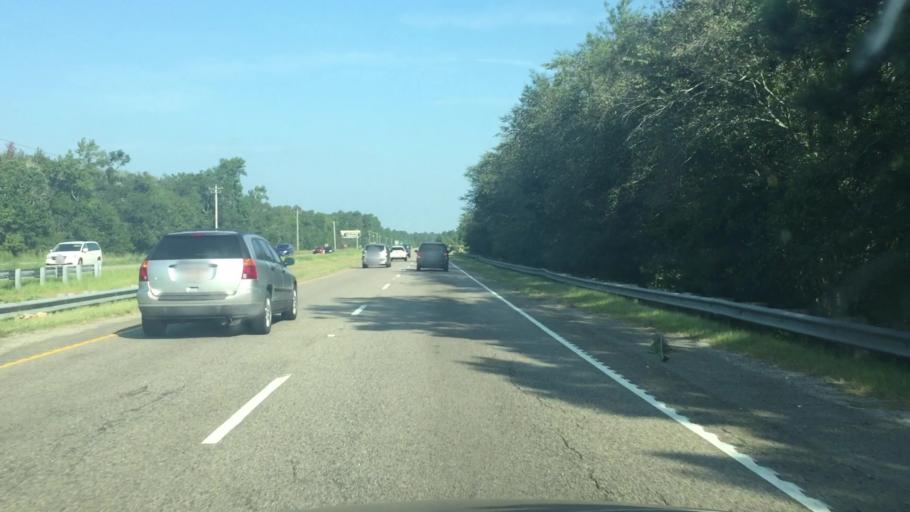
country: US
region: South Carolina
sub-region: Horry County
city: North Myrtle Beach
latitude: 33.9094
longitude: -78.7105
